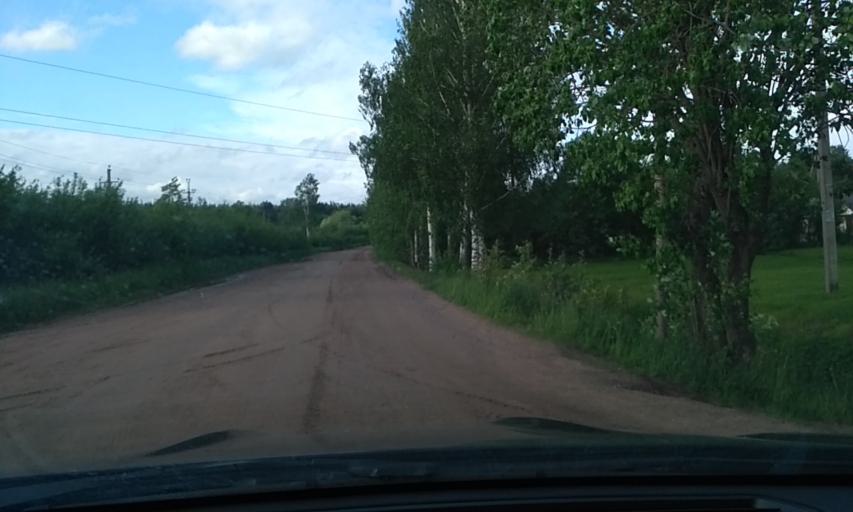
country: RU
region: Leningrad
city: Otradnoye
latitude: 59.8046
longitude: 30.8054
